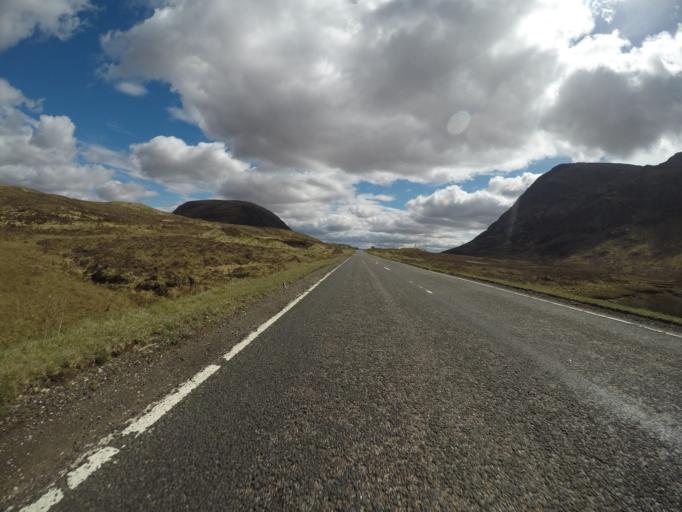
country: GB
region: Scotland
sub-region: Highland
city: Spean Bridge
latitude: 56.6622
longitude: -4.9229
